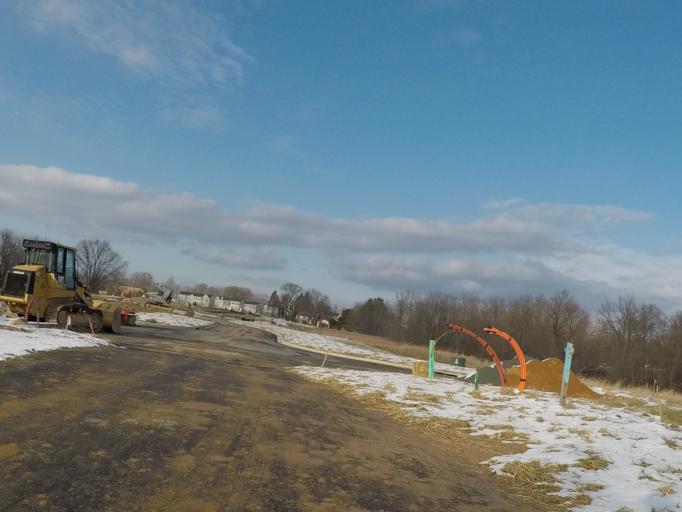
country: US
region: Maryland
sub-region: Howard County
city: Columbia
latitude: 39.2791
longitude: -76.8788
